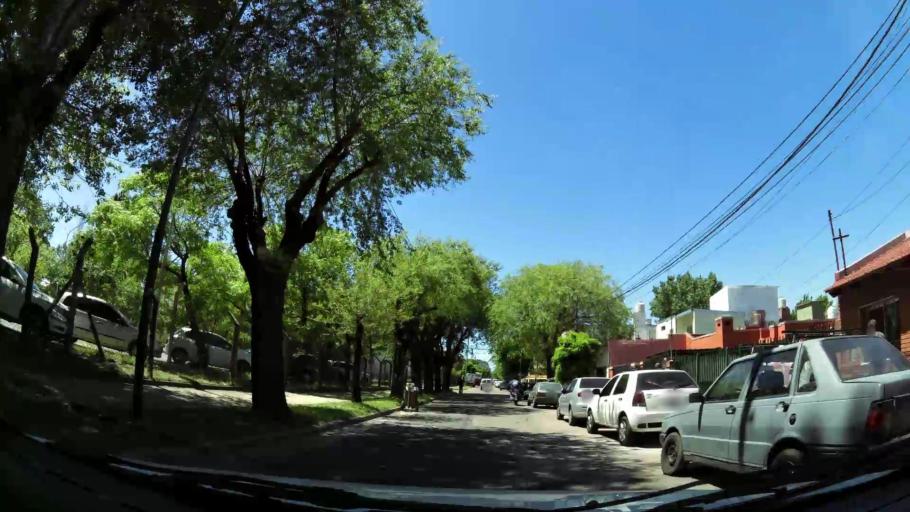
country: AR
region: Buenos Aires
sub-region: Partido de San Isidro
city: San Isidro
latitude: -34.5118
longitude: -58.5497
